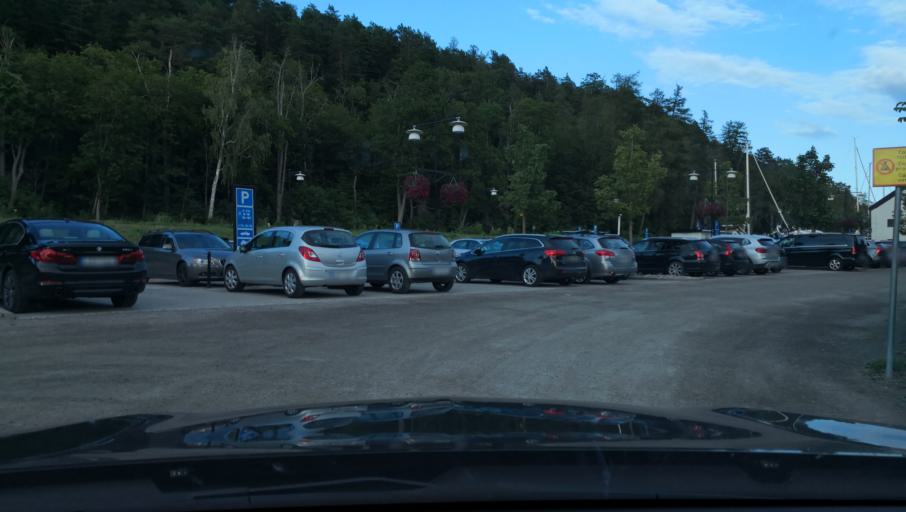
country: SE
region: OEstergoetland
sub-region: Soderkopings Kommun
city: Soederkoeping
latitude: 58.4838
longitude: 16.3196
